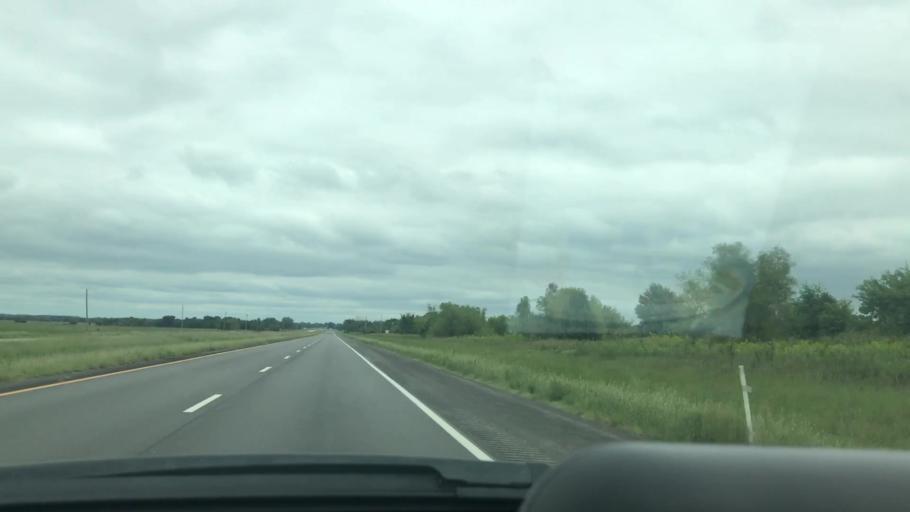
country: US
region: Oklahoma
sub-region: Mayes County
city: Pryor
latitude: 36.4553
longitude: -95.2644
